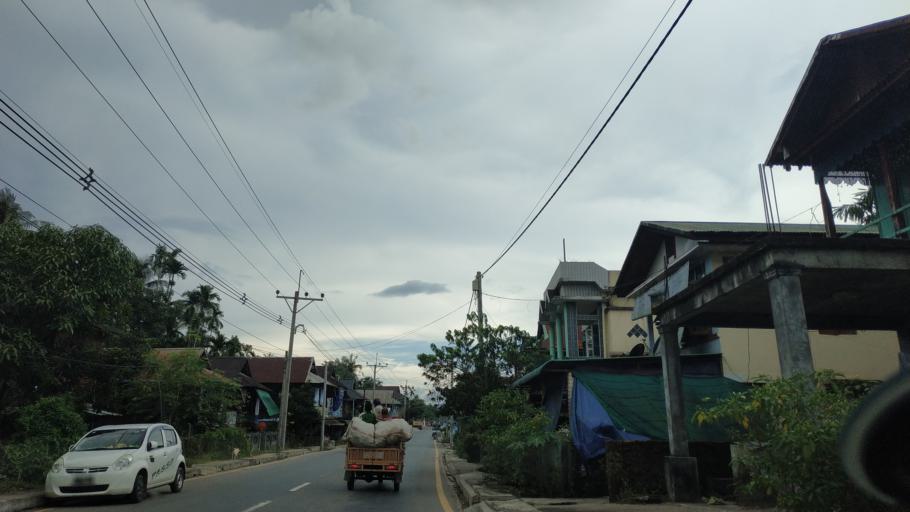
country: MM
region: Tanintharyi
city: Dawei
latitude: 14.0722
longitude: 98.2094
